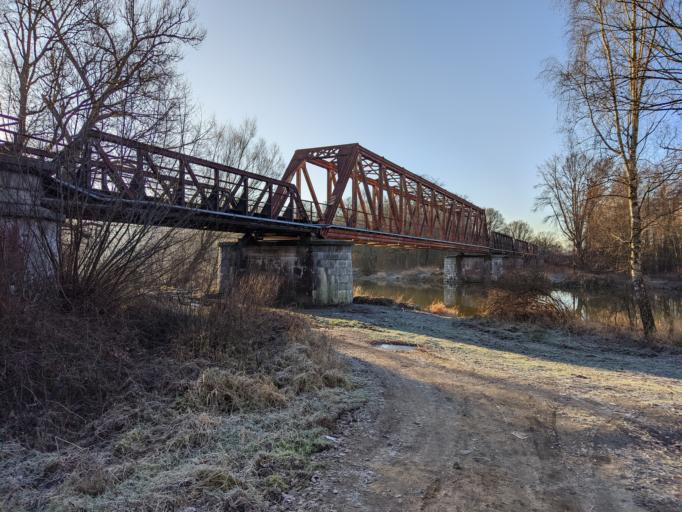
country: PL
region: Lubusz
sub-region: Powiat zielonogorski
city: Nowogrod Bobrzanski
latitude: 51.8079
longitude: 15.2405
